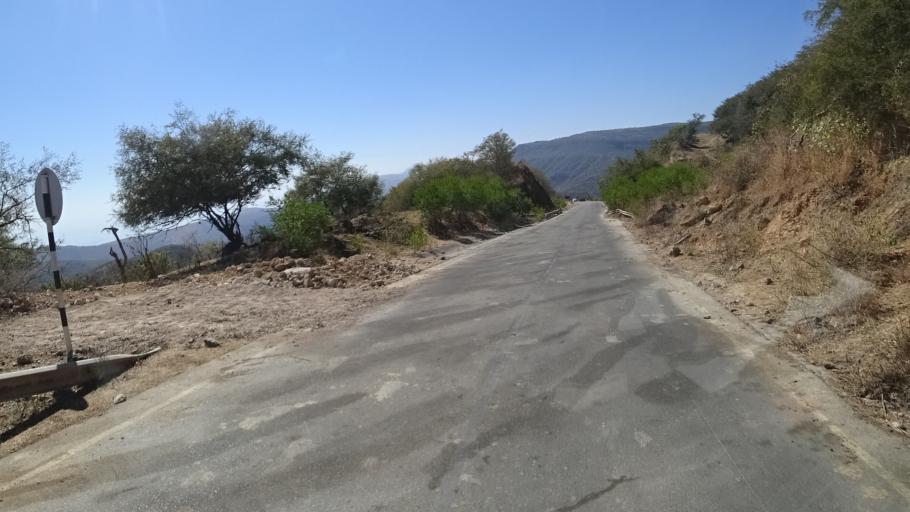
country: YE
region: Al Mahrah
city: Hawf
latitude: 16.7636
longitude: 53.3388
